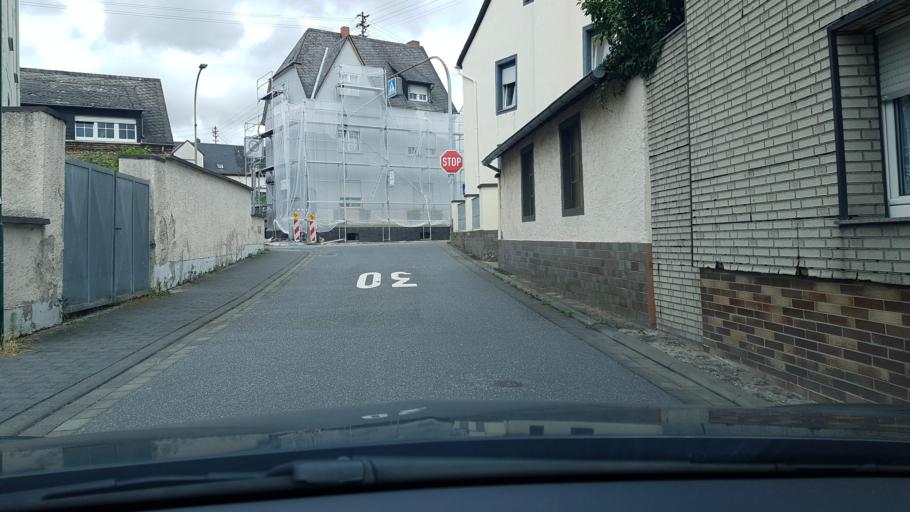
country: DE
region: Rheinland-Pfalz
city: Polch
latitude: 50.3003
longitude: 7.3161
